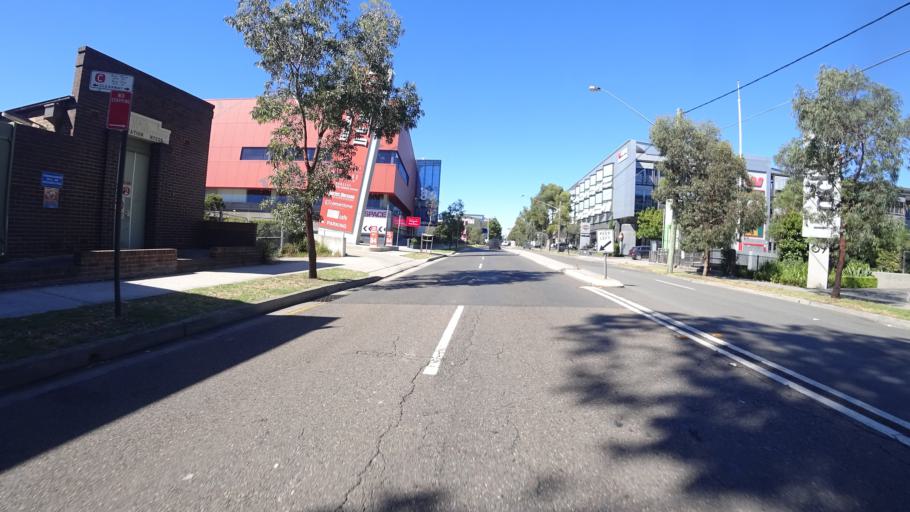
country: AU
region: New South Wales
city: Alexandria
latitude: -33.9172
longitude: 151.1941
